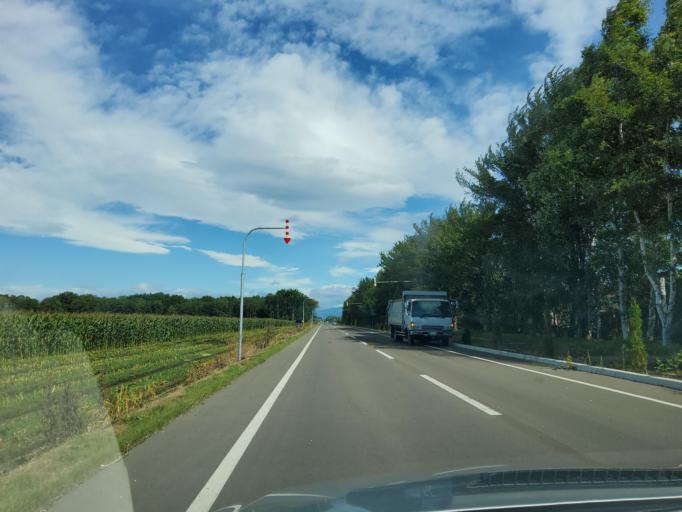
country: JP
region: Hokkaido
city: Otofuke
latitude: 42.9824
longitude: 143.1767
